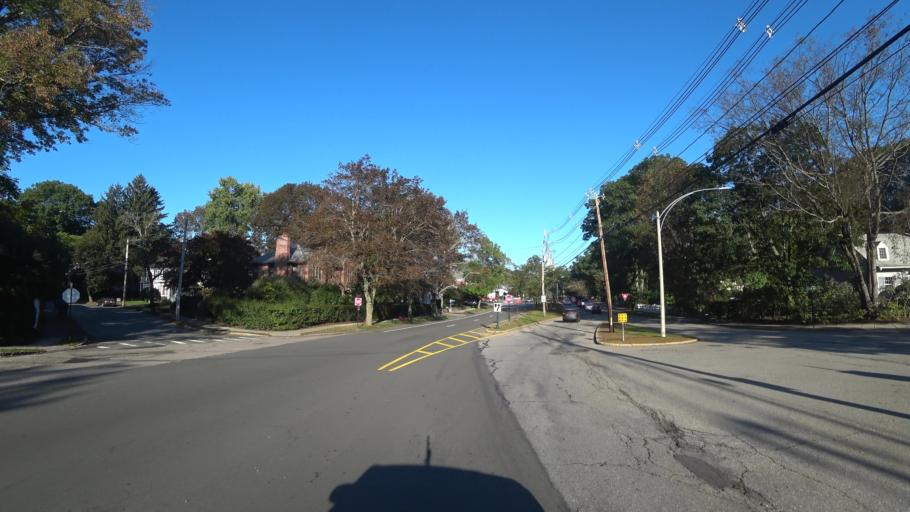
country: US
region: Massachusetts
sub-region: Middlesex County
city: Newton
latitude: 42.3400
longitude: -71.2370
